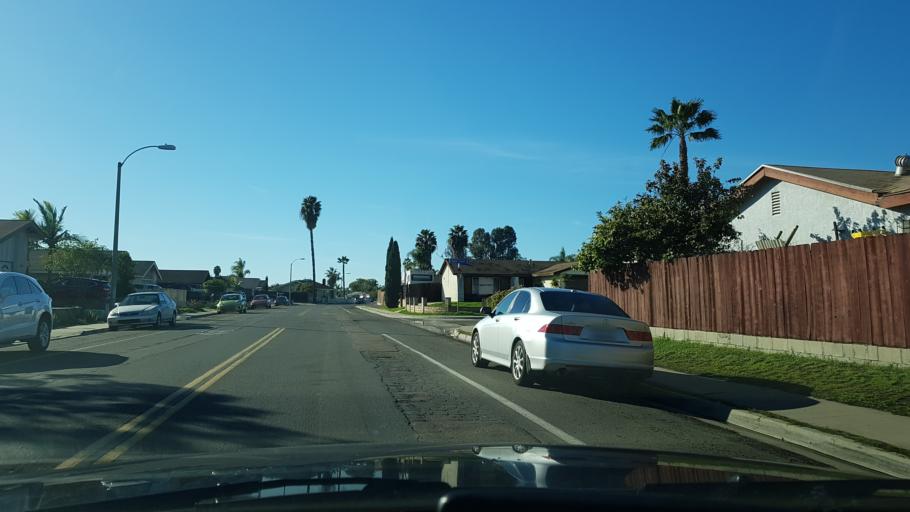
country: US
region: California
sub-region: San Diego County
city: Fairbanks Ranch
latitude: 32.9055
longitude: -117.1335
